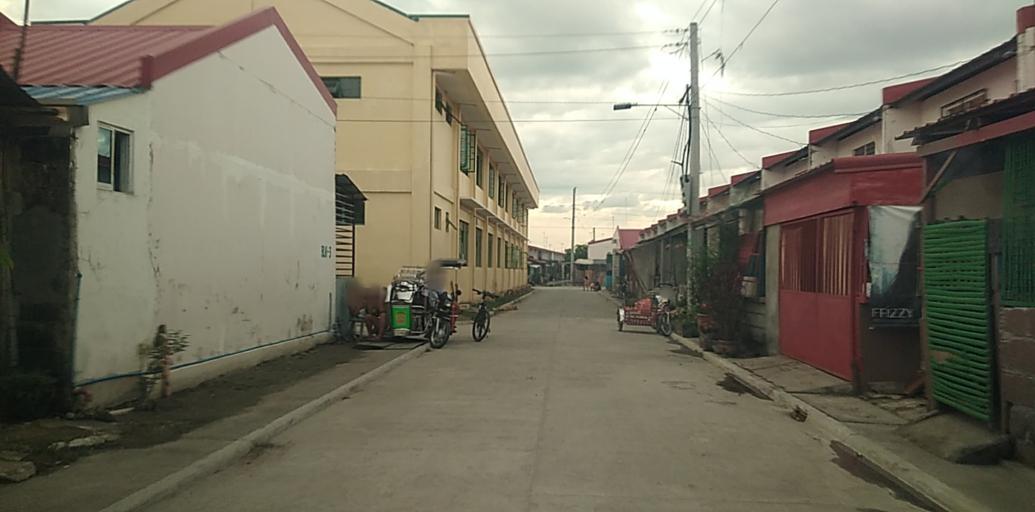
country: PH
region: Central Luzon
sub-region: Province of Pampanga
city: San Fernando
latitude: 15.0102
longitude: 120.7021
